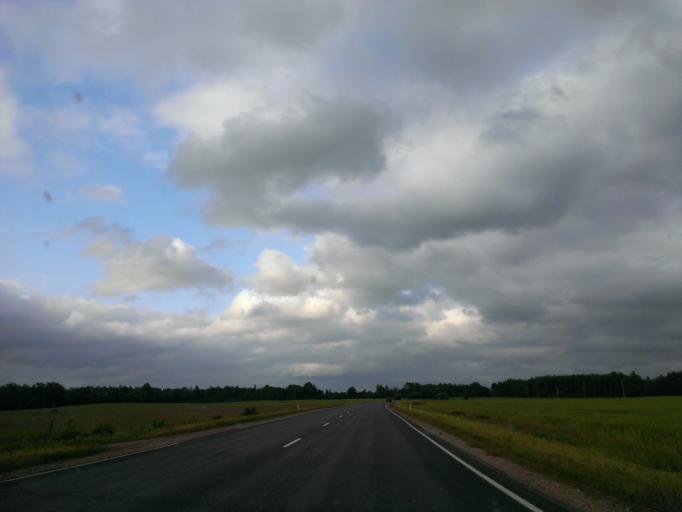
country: LV
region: Skrunda
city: Skrunda
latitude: 56.6814
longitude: 22.1108
